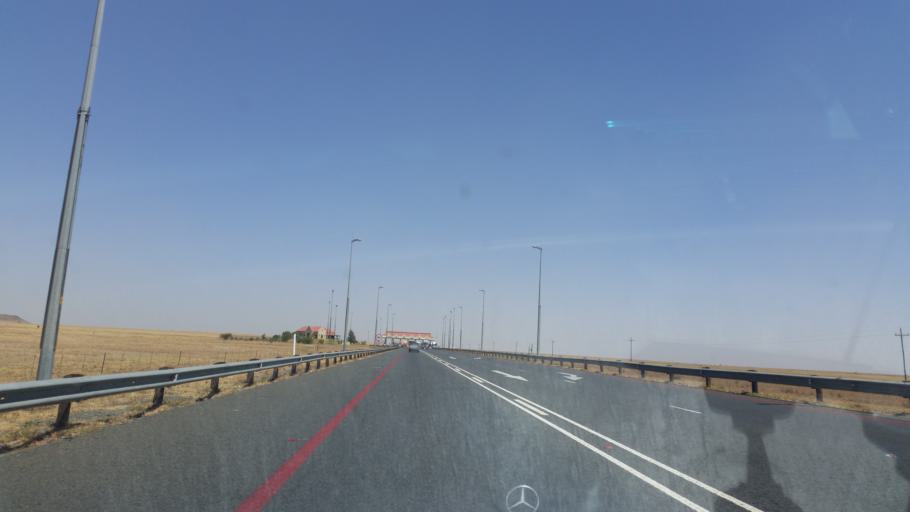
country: ZA
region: Orange Free State
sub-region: Lejweleputswa District Municipality
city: Brandfort
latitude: -28.7957
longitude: 26.6946
